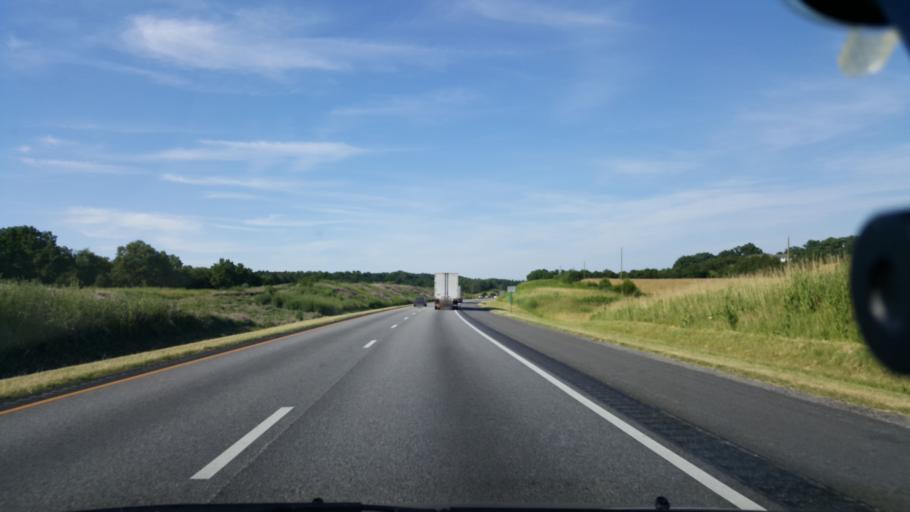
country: US
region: Virginia
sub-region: Augusta County
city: Verona
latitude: 38.2158
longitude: -78.9902
